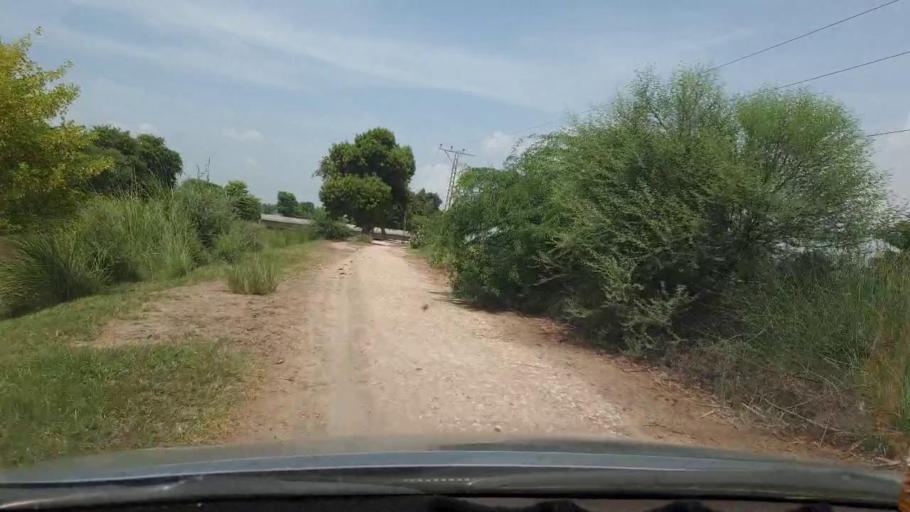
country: PK
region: Sindh
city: Khairpur
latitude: 27.4692
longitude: 68.8063
